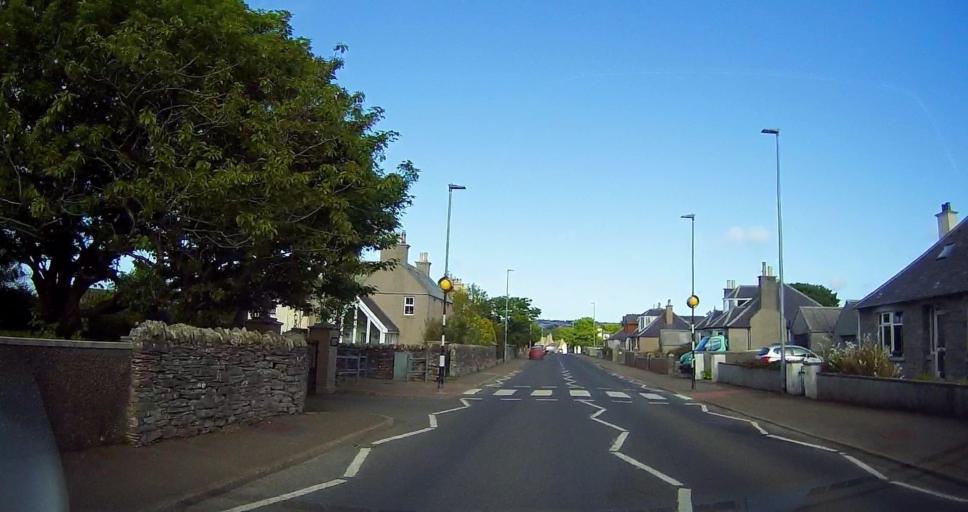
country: GB
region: Scotland
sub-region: Orkney Islands
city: Orkney
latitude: 58.9779
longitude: -2.9723
